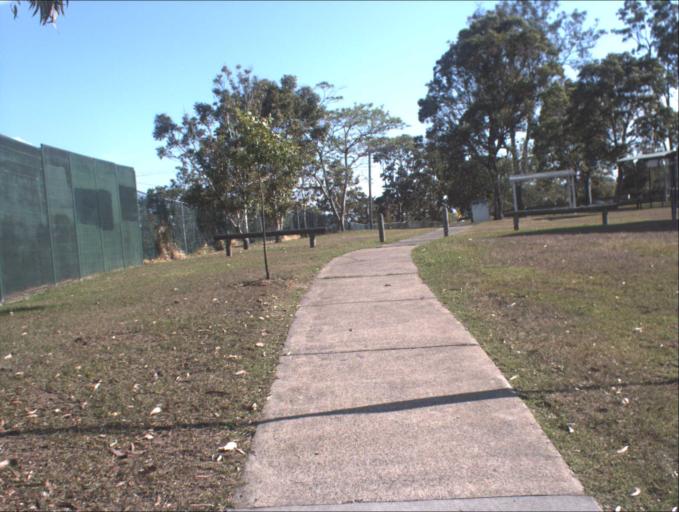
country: AU
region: Queensland
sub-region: Logan
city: Woodridge
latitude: -27.6269
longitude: 153.0998
